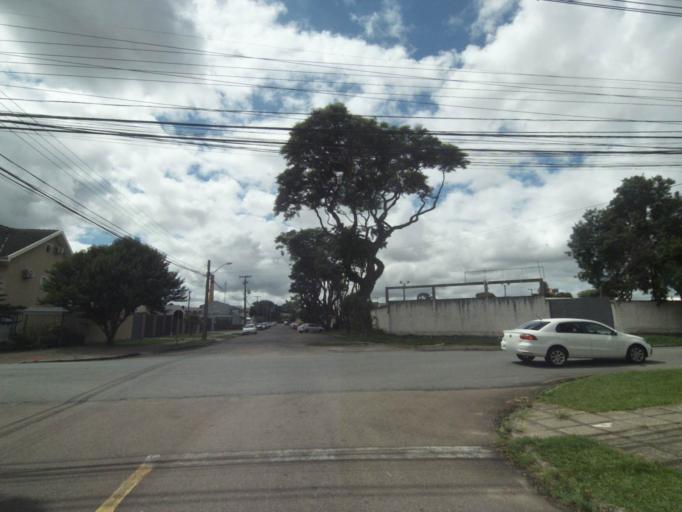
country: BR
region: Parana
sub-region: Curitiba
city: Curitiba
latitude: -25.4789
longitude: -49.2656
